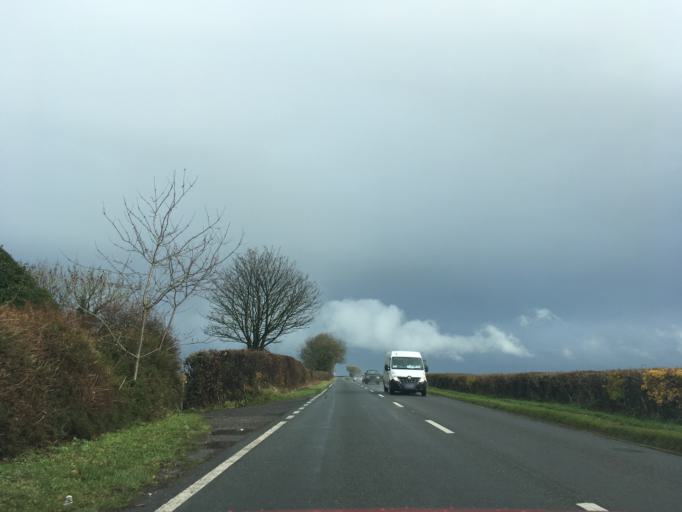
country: GB
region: England
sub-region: South Gloucestershire
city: Cold Ashton
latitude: 51.4559
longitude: -2.3574
